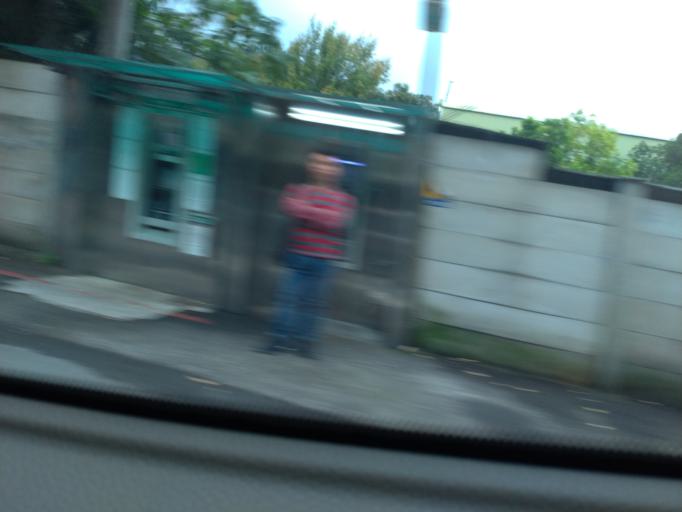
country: TW
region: Taipei
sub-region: Taipei
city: Banqiao
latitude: 24.9289
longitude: 121.4120
